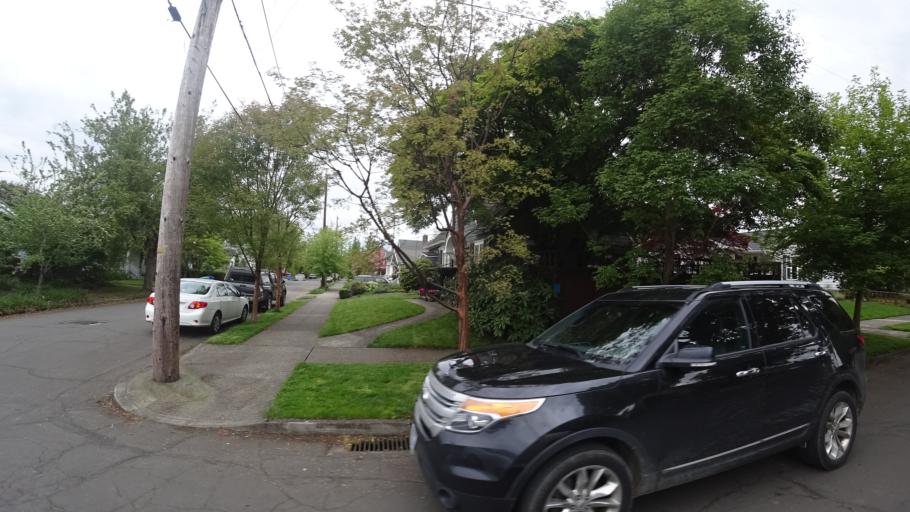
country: US
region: Oregon
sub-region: Clackamas County
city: Milwaukie
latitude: 45.4790
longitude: -122.6444
